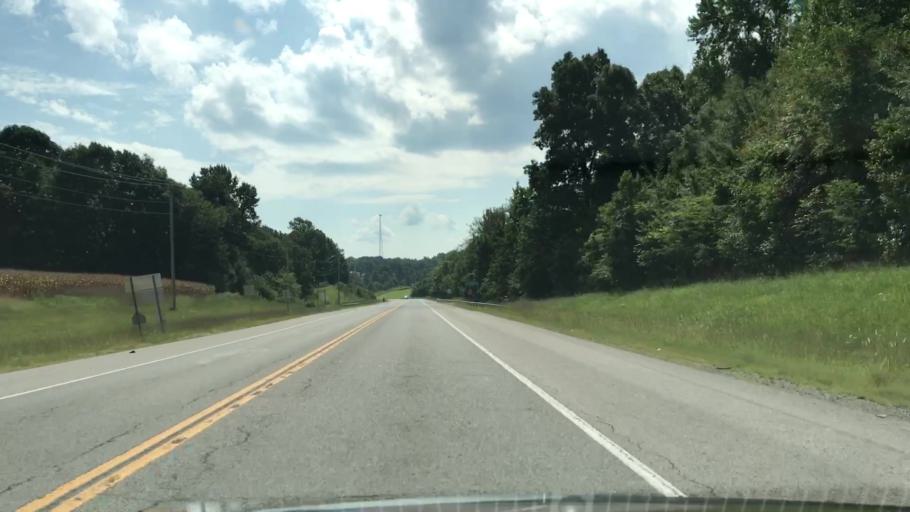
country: US
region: Tennessee
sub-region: Sumner County
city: Westmoreland
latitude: 36.5481
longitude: -86.2229
